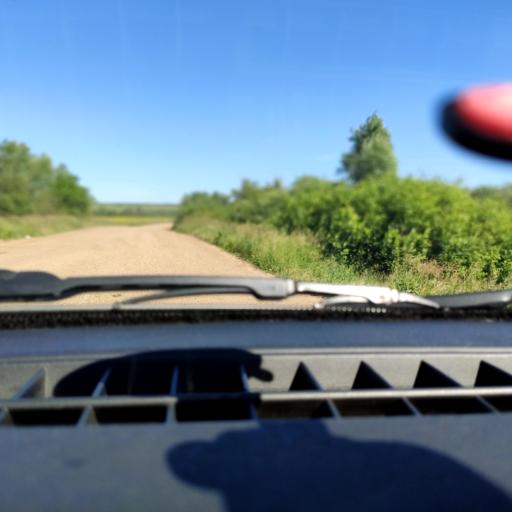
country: RU
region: Bashkortostan
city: Iglino
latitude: 54.9071
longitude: 56.4763
